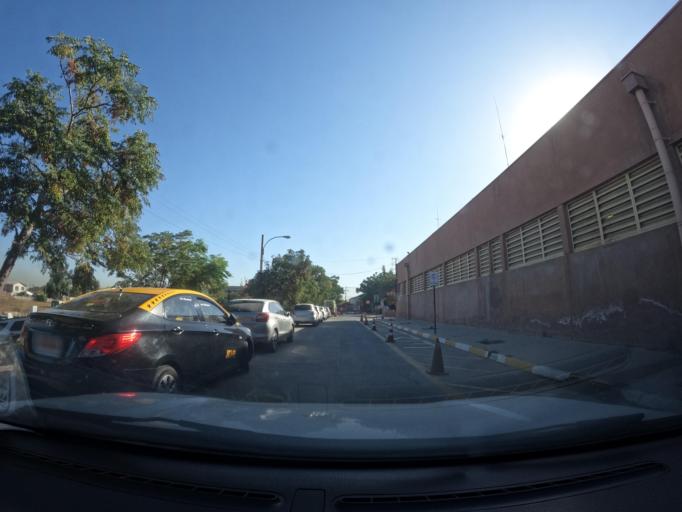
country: CL
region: Santiago Metropolitan
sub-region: Provincia de Santiago
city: Villa Presidente Frei, Nunoa, Santiago, Chile
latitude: -33.4999
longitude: -70.5795
